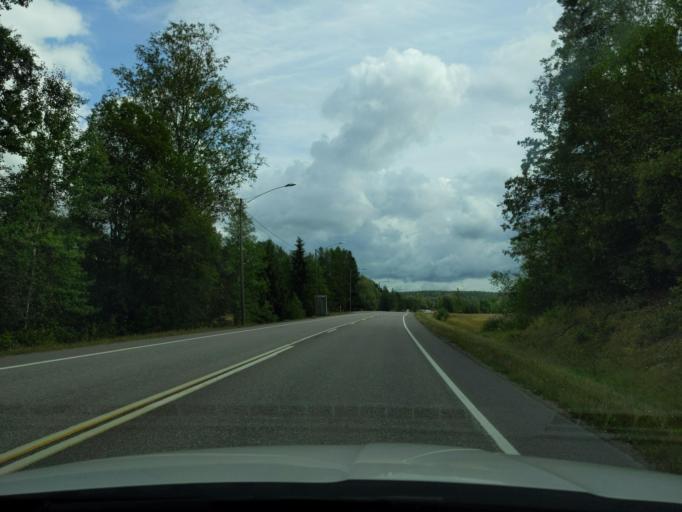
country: FI
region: Uusimaa
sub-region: Porvoo
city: Porvoo
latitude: 60.4545
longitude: 25.7394
